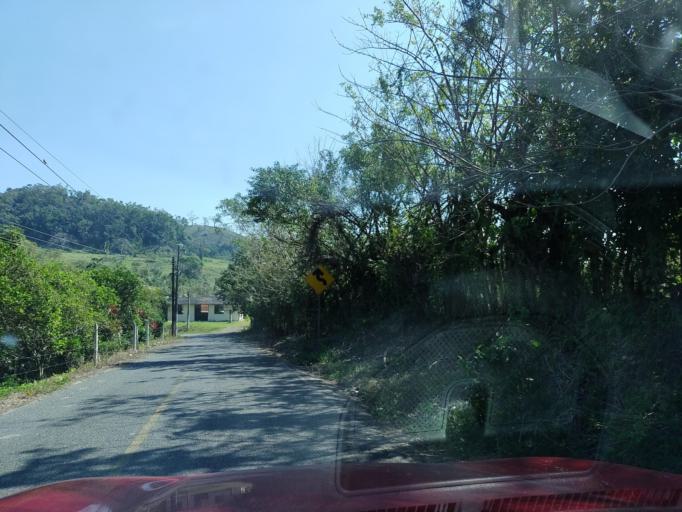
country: MX
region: Veracruz
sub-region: Papantla
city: Polutla
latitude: 20.5004
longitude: -97.2162
